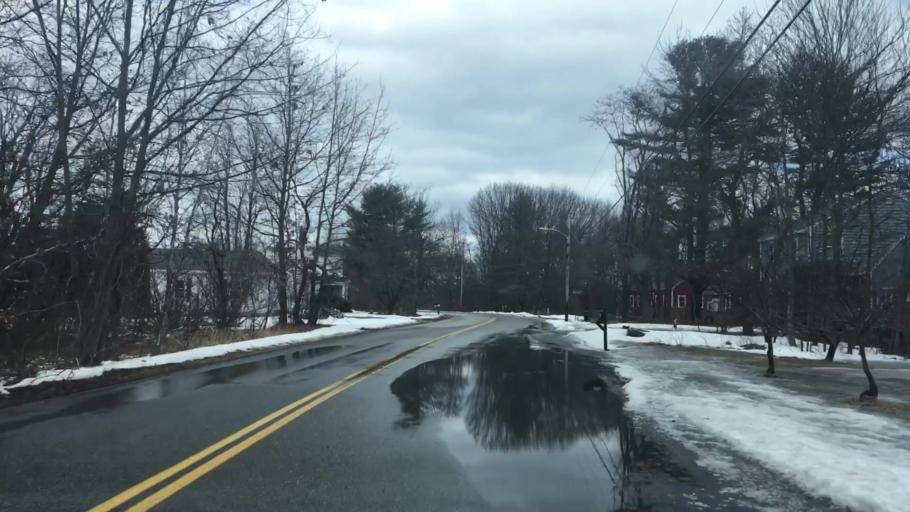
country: US
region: Maine
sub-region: York County
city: Wells Beach Station
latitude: 43.3082
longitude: -70.6548
